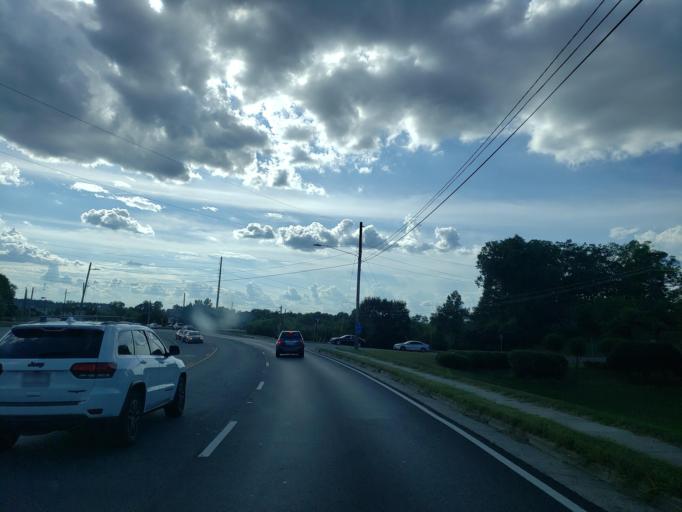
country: US
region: Georgia
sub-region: Floyd County
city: Rome
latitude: 34.2605
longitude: -85.1666
